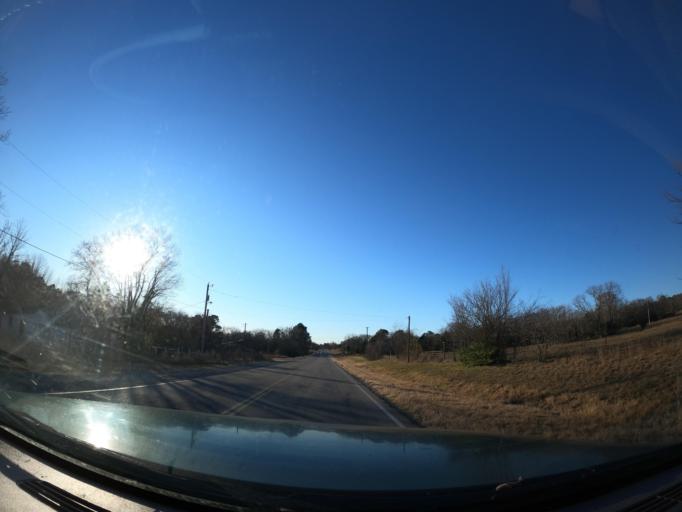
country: US
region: Oklahoma
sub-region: Pittsburg County
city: Hartshorne
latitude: 34.8876
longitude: -95.4712
